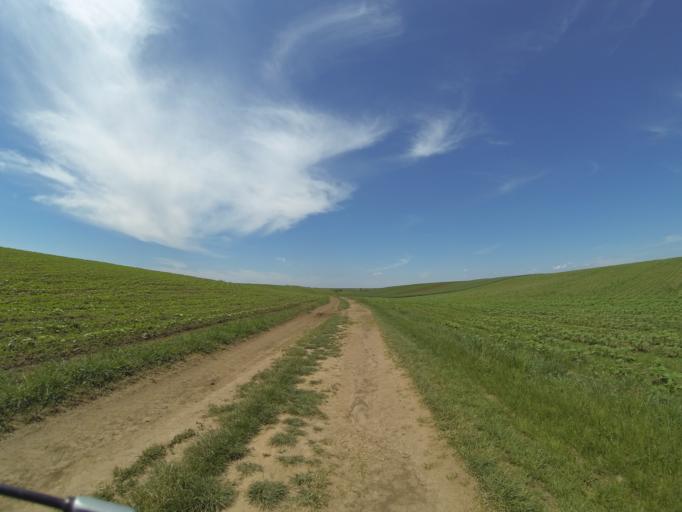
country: RO
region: Dolj
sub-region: Comuna Teslui
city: Teslui
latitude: 44.1916
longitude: 24.1474
